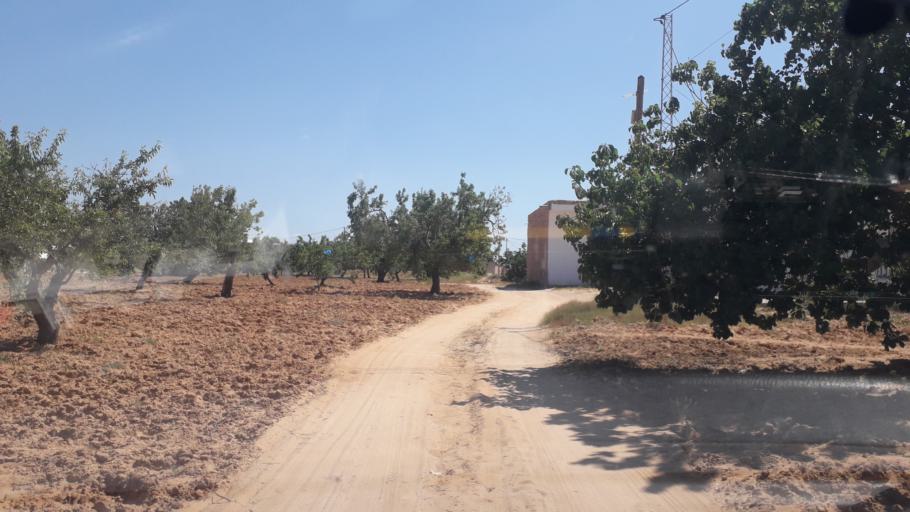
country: TN
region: Safaqis
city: Al Qarmadah
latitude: 34.8330
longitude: 10.7703
